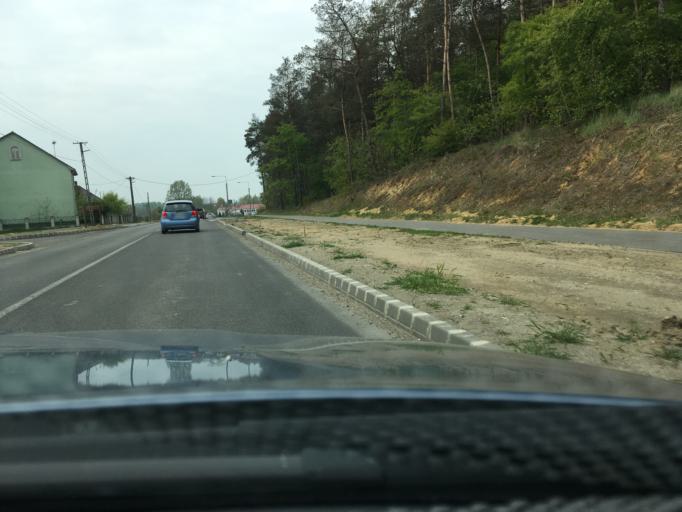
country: HU
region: Hajdu-Bihar
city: Nyiradony
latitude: 47.6842
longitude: 21.8893
